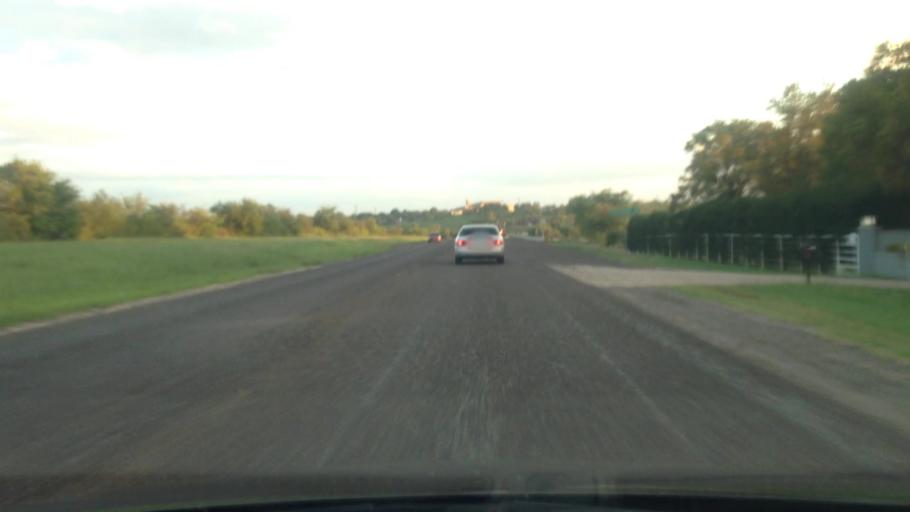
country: US
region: Texas
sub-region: Tarrant County
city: Benbrook
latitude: 32.6842
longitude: -97.4991
